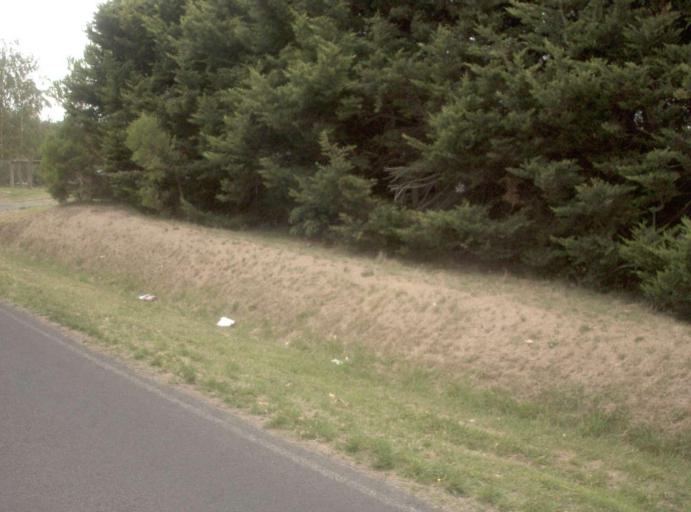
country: AU
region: Victoria
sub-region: Baw Baw
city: Warragul
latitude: -38.1167
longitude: 145.8343
